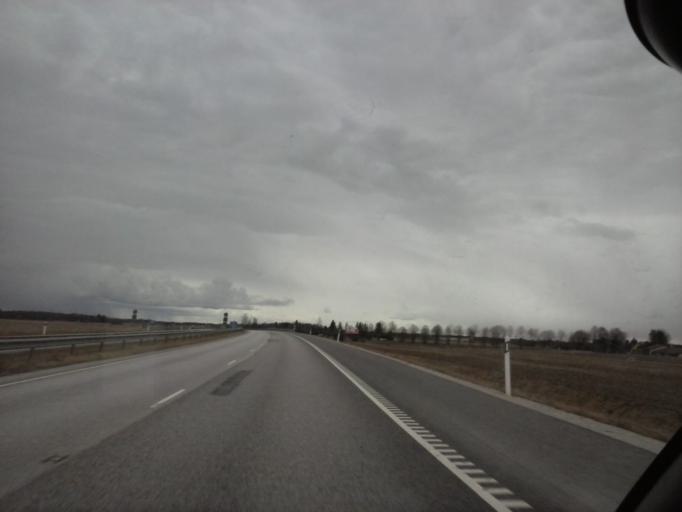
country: EE
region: Jaervamaa
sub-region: Paide linn
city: Paide
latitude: 58.9340
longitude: 25.6100
